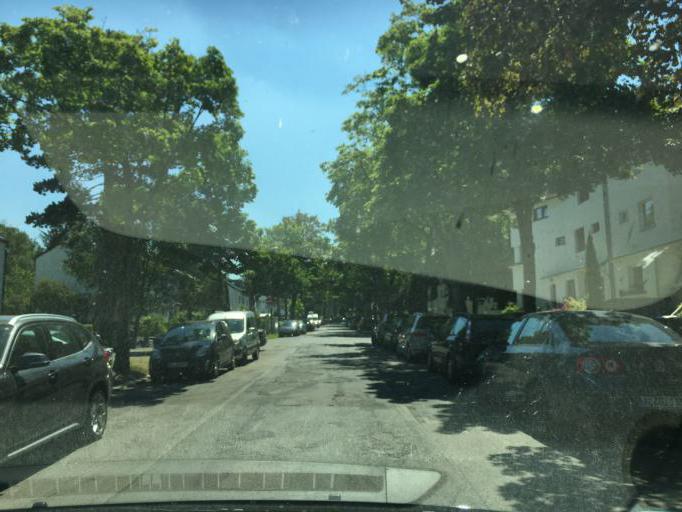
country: DE
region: North Rhine-Westphalia
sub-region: Regierungsbezirk Koln
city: Aachen
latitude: 50.7550
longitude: 6.0912
